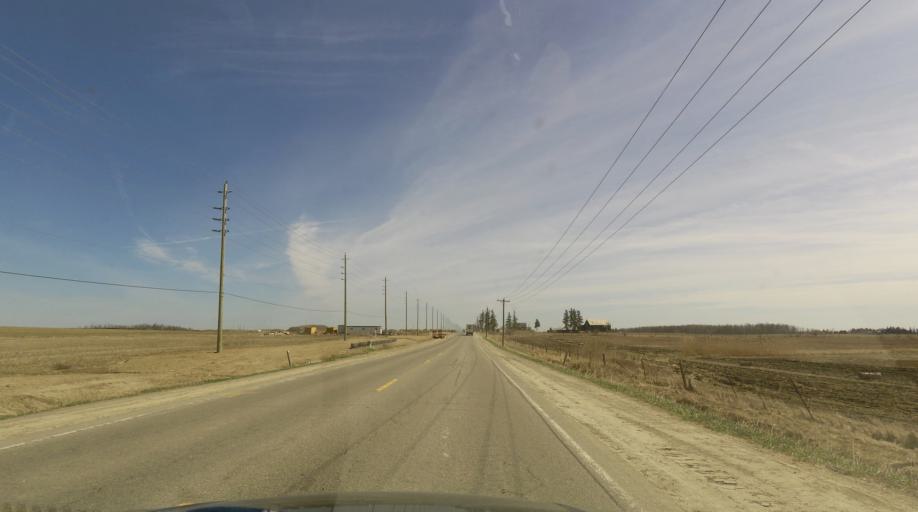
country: CA
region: Ontario
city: Brampton
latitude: 43.6919
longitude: -79.8635
